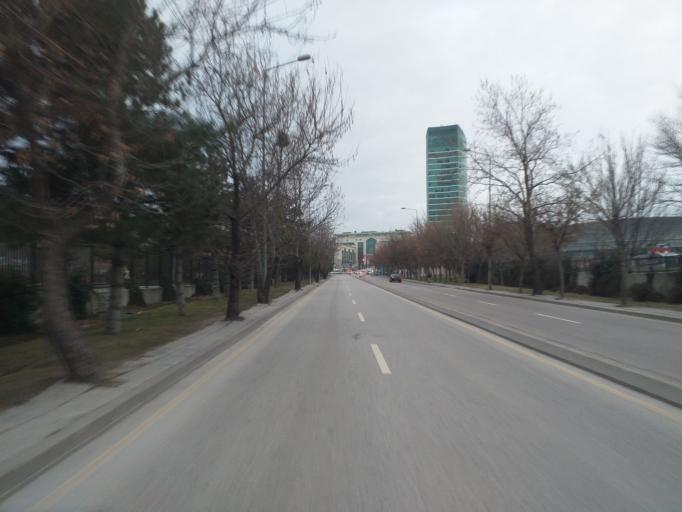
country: TR
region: Ankara
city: Ankara
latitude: 39.9665
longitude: 32.8198
